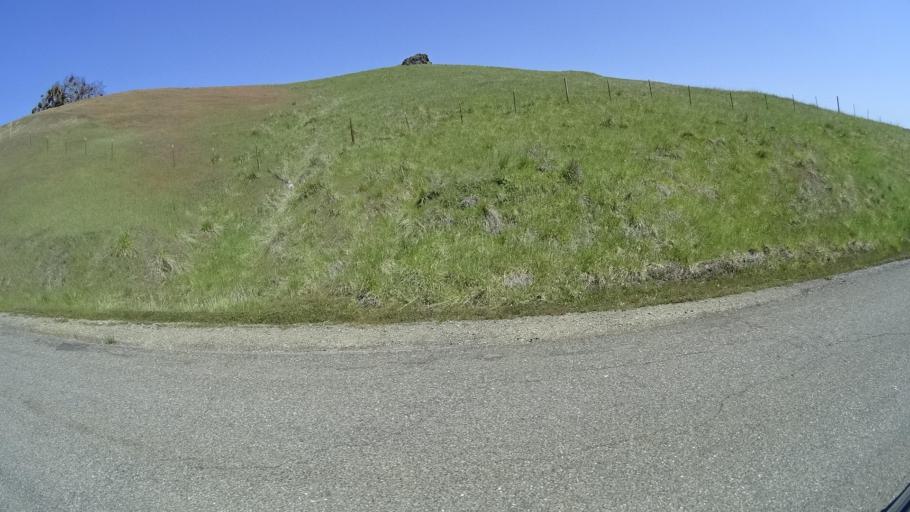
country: US
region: California
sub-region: Humboldt County
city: Redway
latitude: 40.1040
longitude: -123.6802
